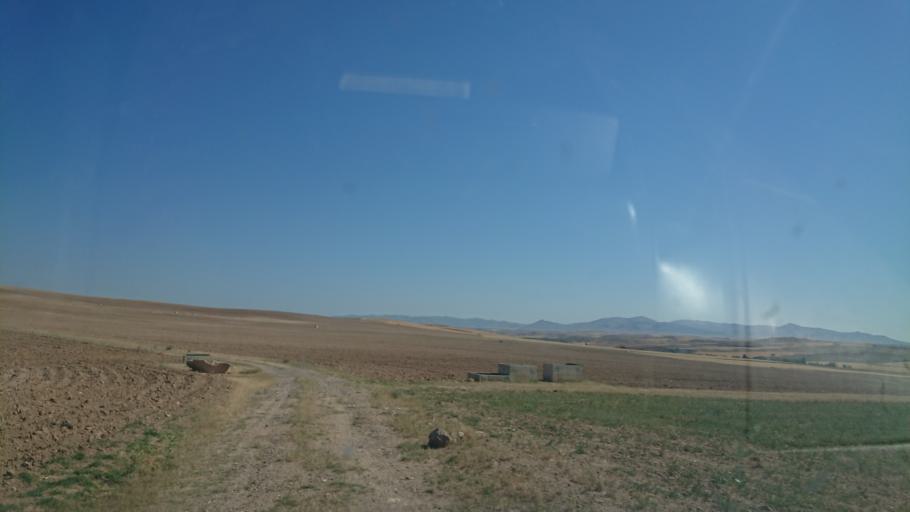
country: TR
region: Aksaray
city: Sariyahsi
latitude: 39.0493
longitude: 33.8903
